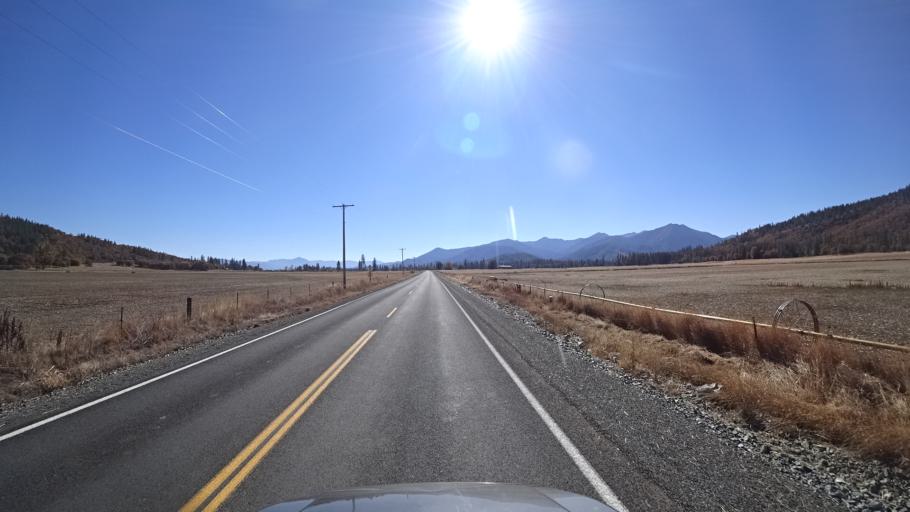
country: US
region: California
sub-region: Siskiyou County
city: Yreka
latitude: 41.5649
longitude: -122.9233
